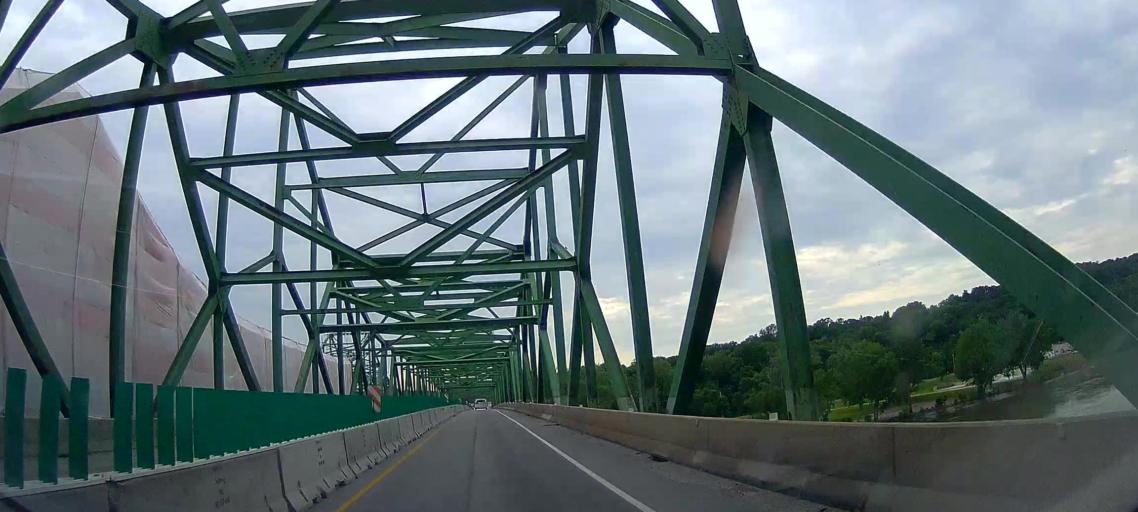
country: US
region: Iowa
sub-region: Pottawattamie County
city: Carter Lake
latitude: 41.3460
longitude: -95.9568
